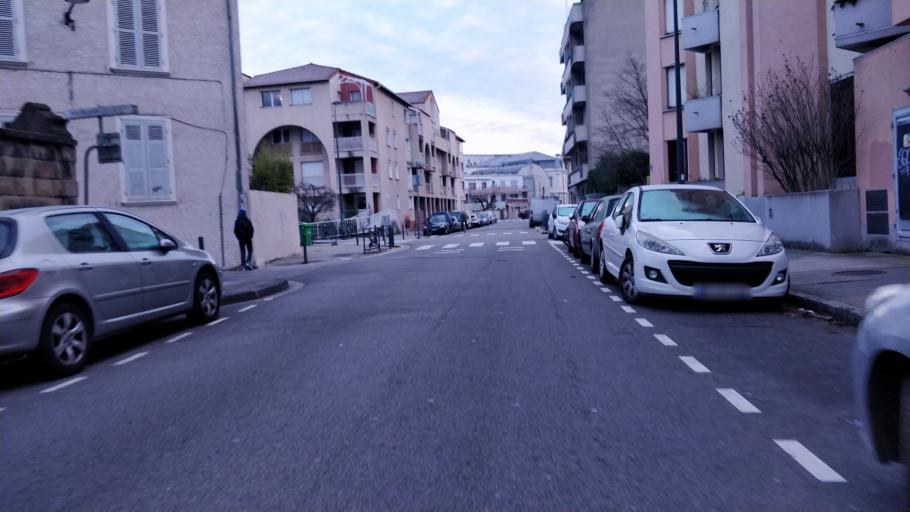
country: FR
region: Rhone-Alpes
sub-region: Departement de l'Isere
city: Seyssinet-Pariset
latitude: 45.1842
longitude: 5.7090
